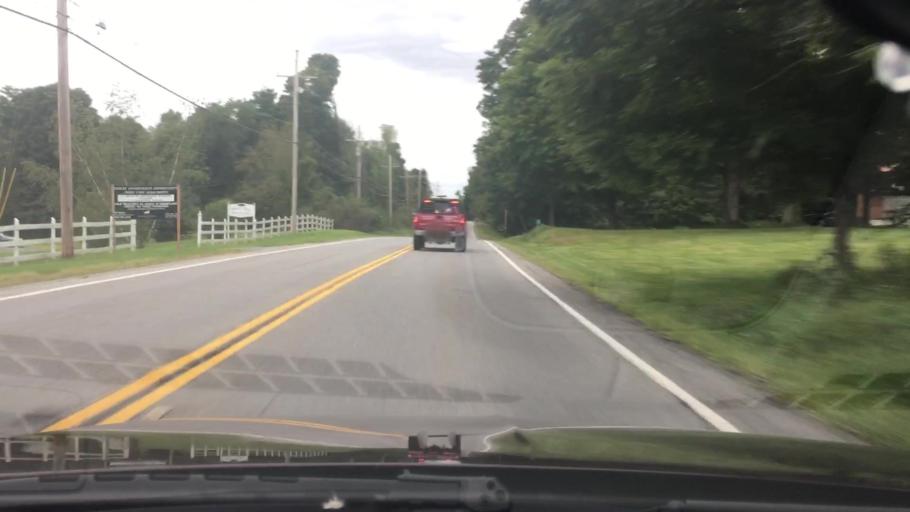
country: US
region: New York
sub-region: Dutchess County
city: Pleasant Valley
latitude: 41.7631
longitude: -73.7806
